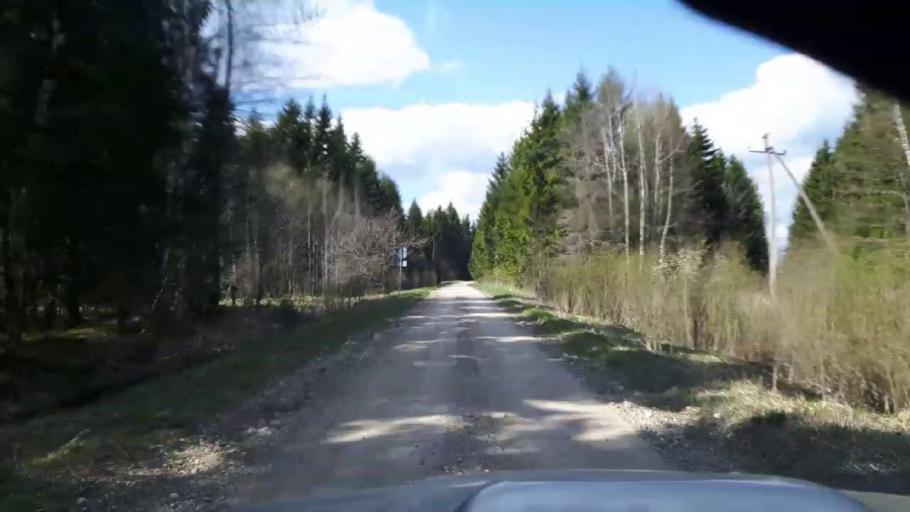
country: EE
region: Paernumaa
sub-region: Tootsi vald
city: Tootsi
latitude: 58.4468
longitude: 24.9053
